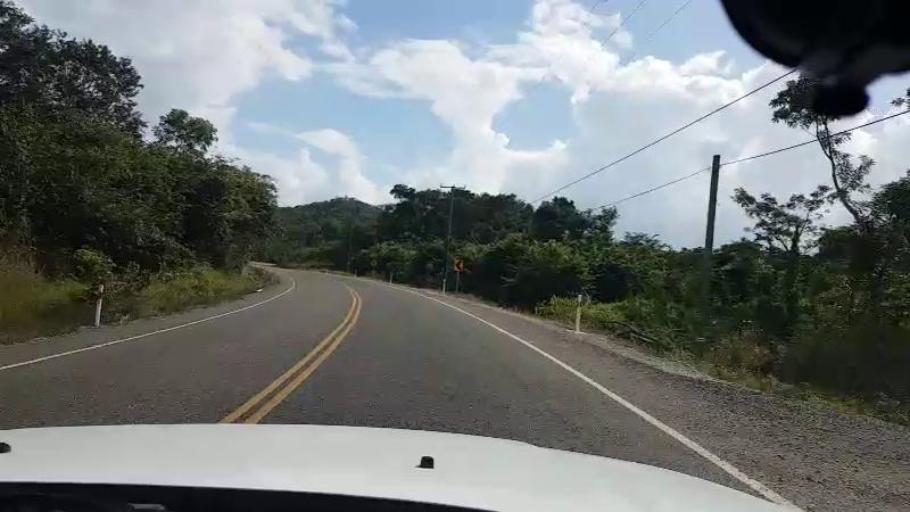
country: BZ
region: Cayo
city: Belmopan
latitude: 17.2272
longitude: -88.7794
